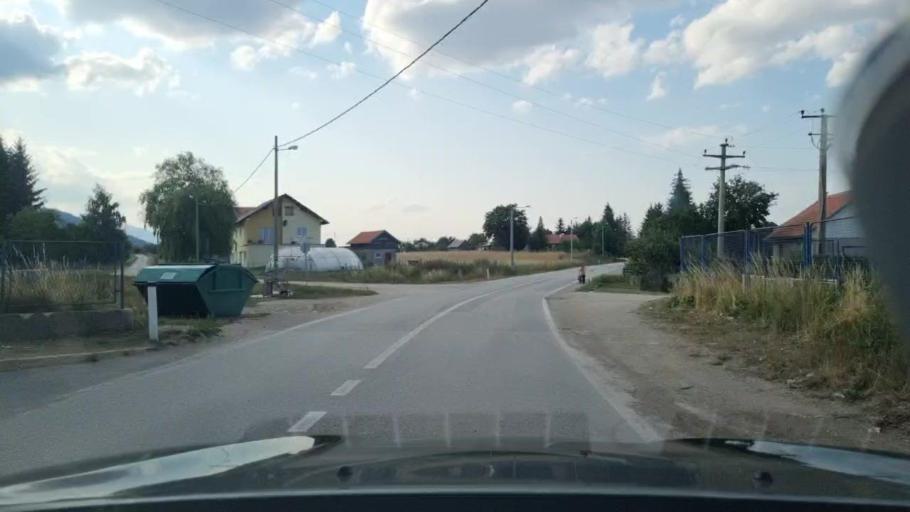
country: BA
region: Federation of Bosnia and Herzegovina
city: Glamoc
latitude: 44.0546
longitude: 16.8312
